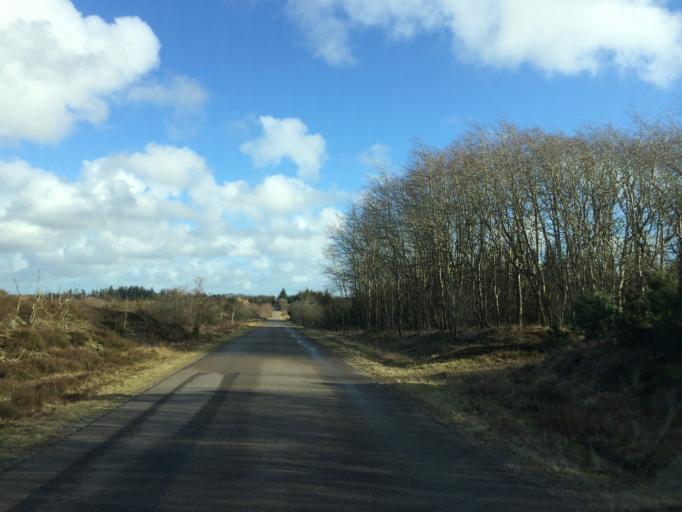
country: DK
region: Central Jutland
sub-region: Holstebro Kommune
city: Ulfborg
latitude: 56.2398
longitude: 8.4058
